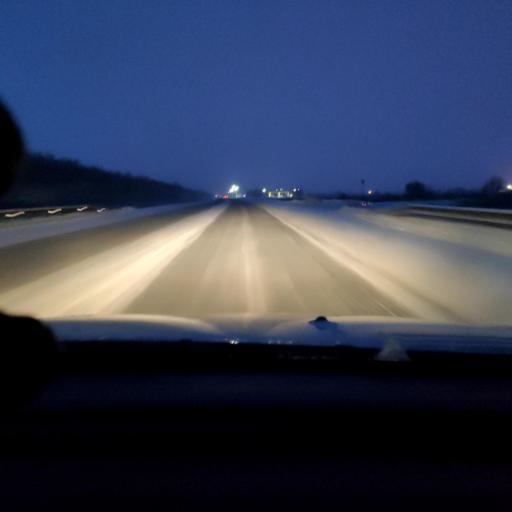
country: RU
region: Samara
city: Kinel'-Cherkassy
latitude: 53.4036
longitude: 51.4253
